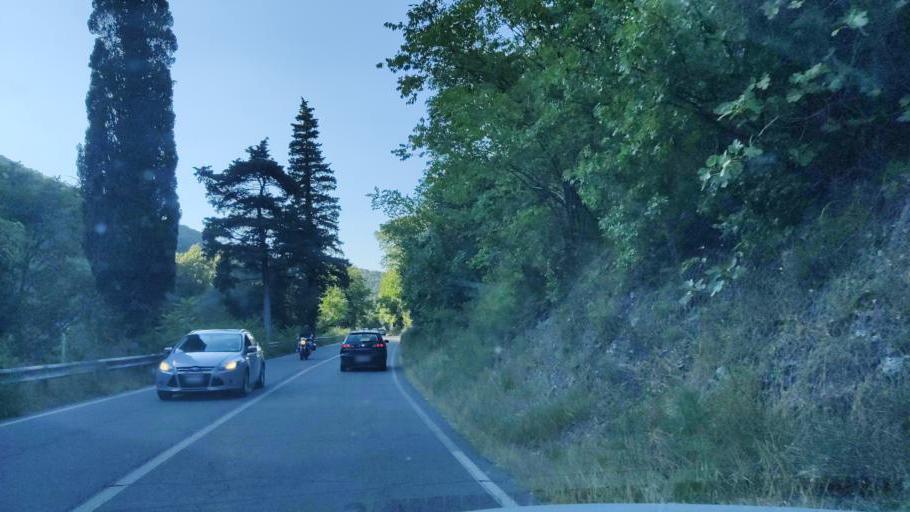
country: IT
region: Umbria
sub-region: Provincia di Terni
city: Narni
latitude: 42.5164
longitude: 12.5133
